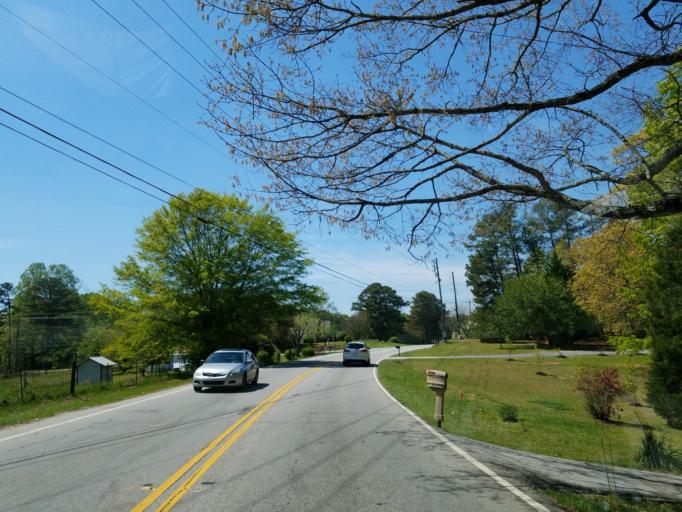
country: US
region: Georgia
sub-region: Paulding County
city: Hiram
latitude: 33.8654
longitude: -84.8019
